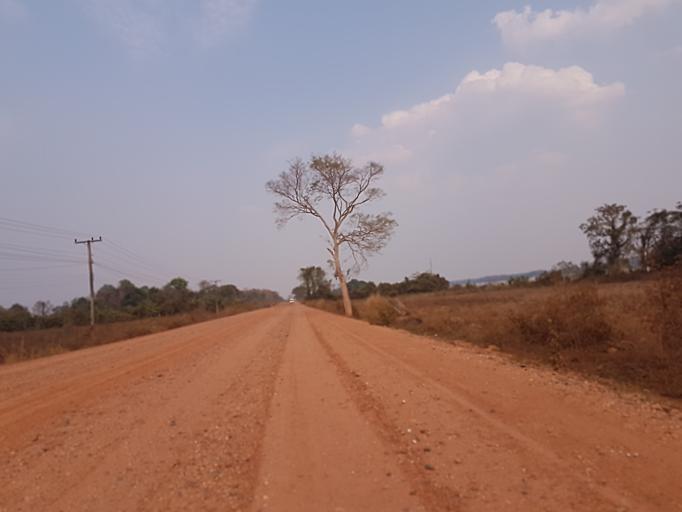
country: TH
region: Nong Khai
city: Nong Khai
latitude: 17.9773
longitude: 102.8642
